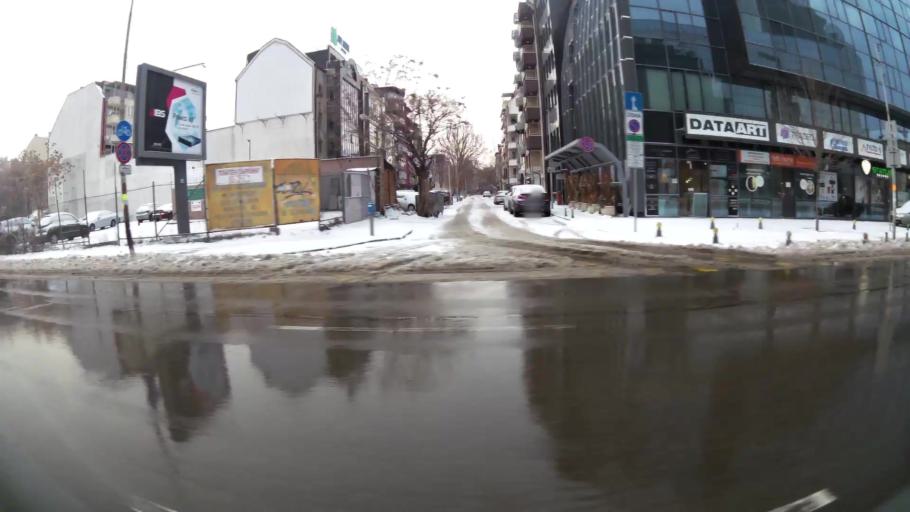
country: BG
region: Sofia-Capital
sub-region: Stolichna Obshtina
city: Sofia
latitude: 42.7003
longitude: 23.3081
